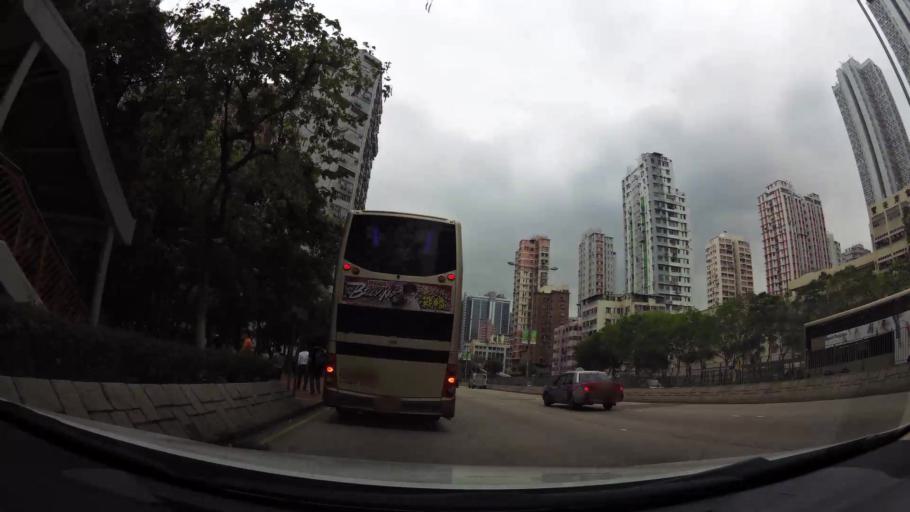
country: HK
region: Tsuen Wan
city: Tsuen Wan
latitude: 22.3716
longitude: 114.1095
